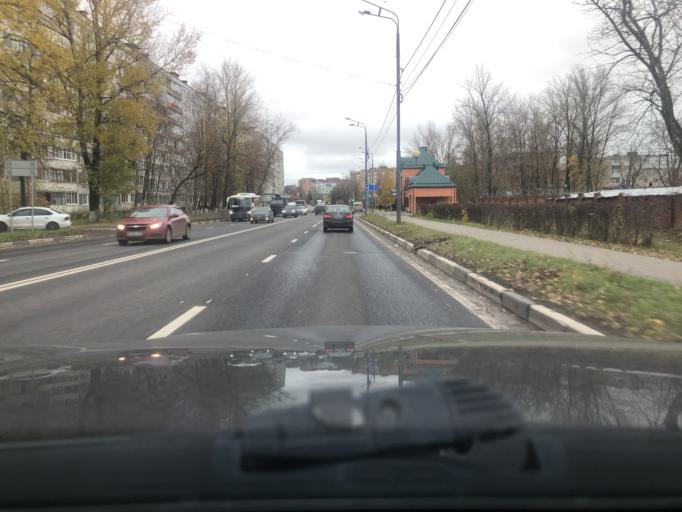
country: RU
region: Moskovskaya
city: Sergiyev Posad
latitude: 56.3310
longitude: 38.1314
